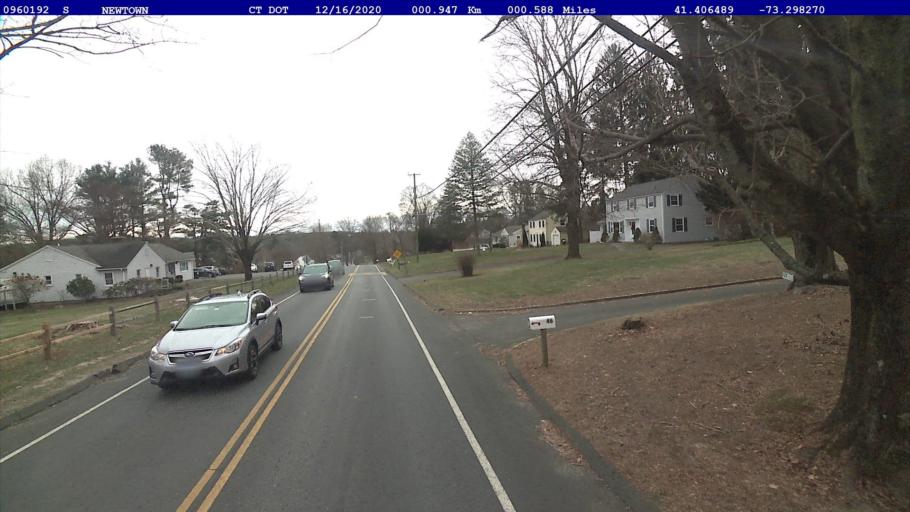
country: US
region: Connecticut
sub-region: Fairfield County
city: Newtown
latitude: 41.4065
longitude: -73.2983
